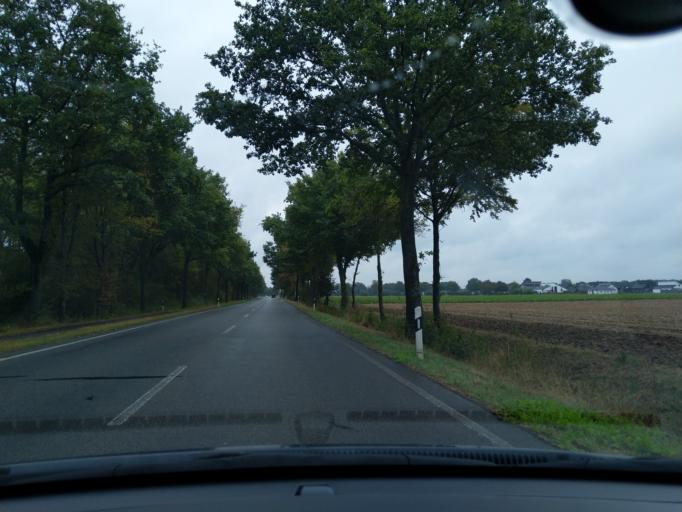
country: DE
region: North Rhine-Westphalia
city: Erkelenz
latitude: 51.0592
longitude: 6.3084
